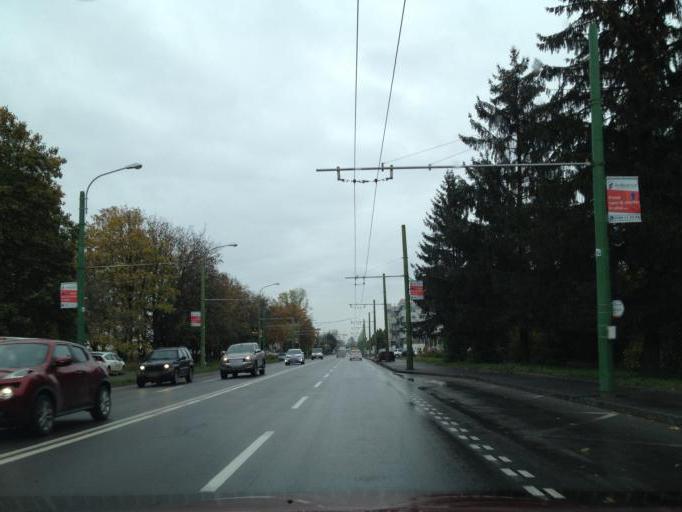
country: RO
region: Brasov
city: Brasov
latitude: 45.6774
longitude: 25.6137
